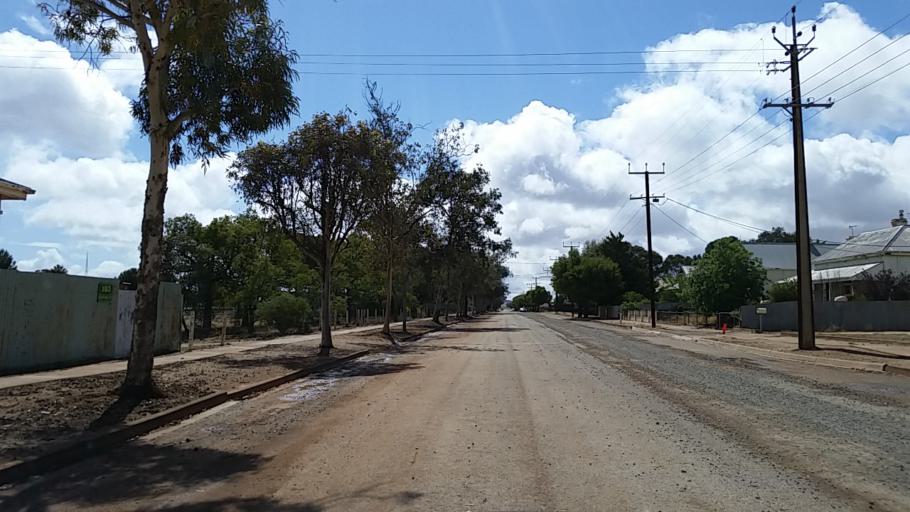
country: AU
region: South Australia
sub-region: Peterborough
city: Peterborough
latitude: -32.9749
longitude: 138.8339
